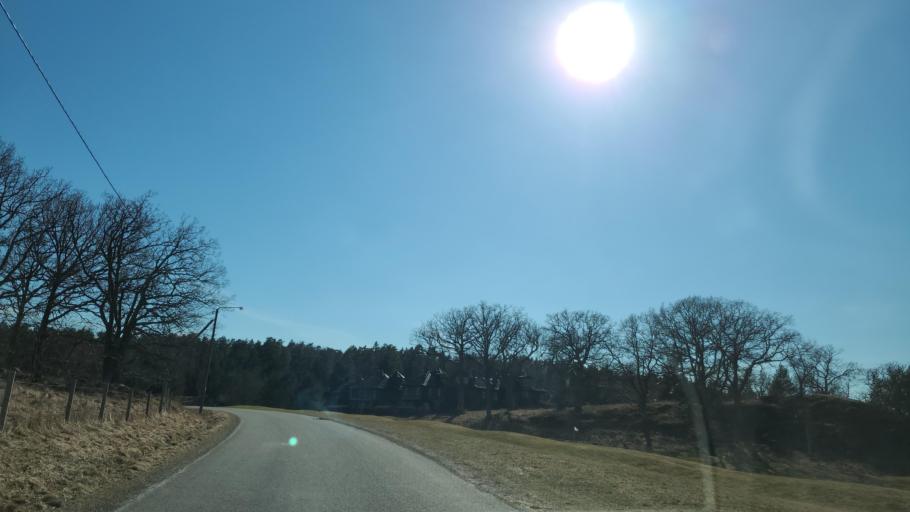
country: SE
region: Stockholm
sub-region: Varmdo Kommun
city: Hemmesta
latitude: 59.2765
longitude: 18.5480
